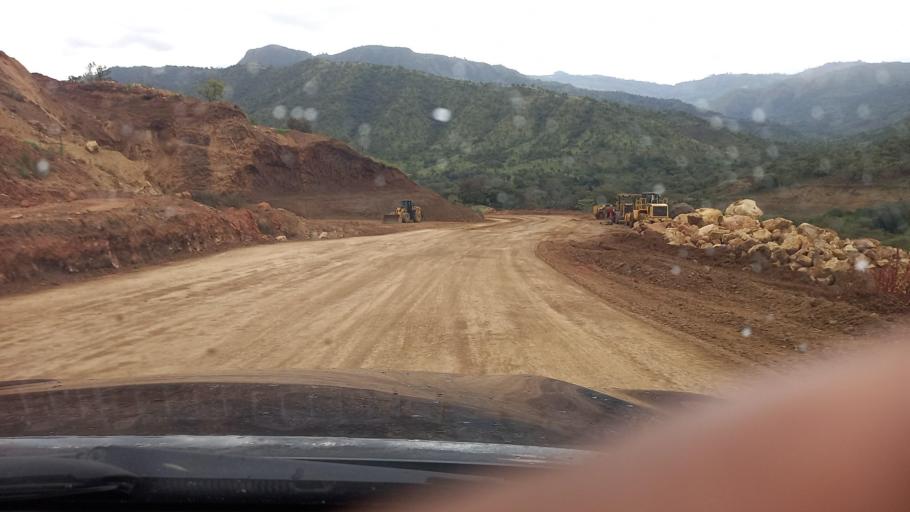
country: ET
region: Southern Nations, Nationalities, and People's Region
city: Mizan Teferi
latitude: 6.1910
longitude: 35.6784
